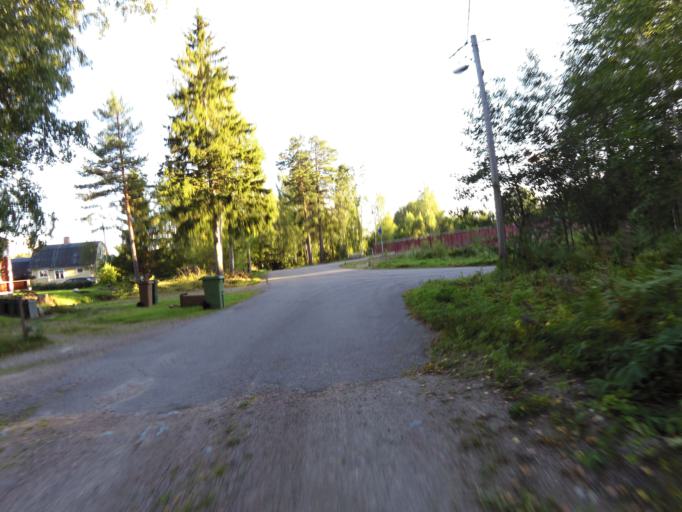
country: SE
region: Gaevleborg
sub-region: Gavle Kommun
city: Gavle
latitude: 60.7184
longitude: 17.1418
